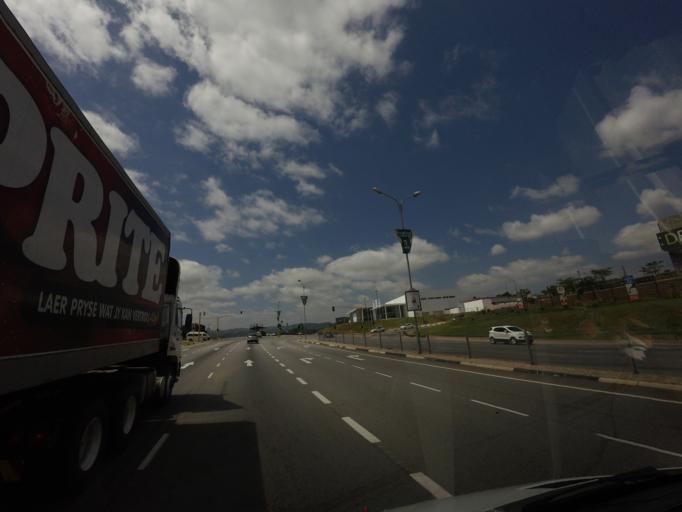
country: ZA
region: Mpumalanga
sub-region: Ehlanzeni District
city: Nelspruit
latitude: -25.4347
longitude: 30.9654
